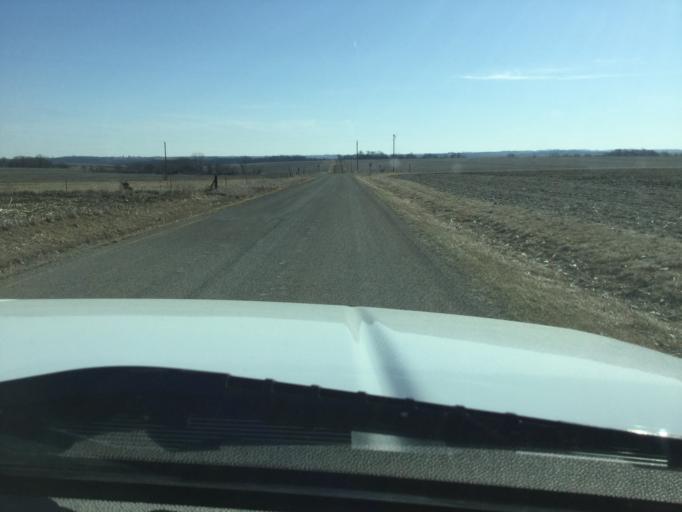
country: US
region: Kansas
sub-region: Brown County
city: Horton
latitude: 39.7256
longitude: -95.4360
